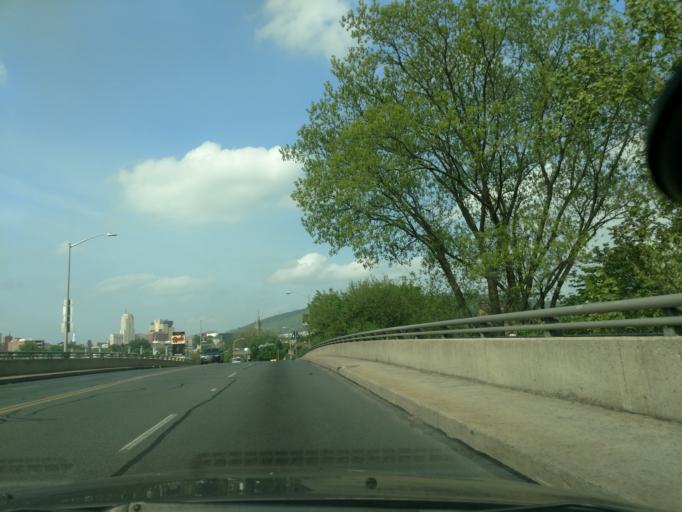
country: US
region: Pennsylvania
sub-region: Berks County
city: Reading
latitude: 40.3260
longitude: -75.9323
